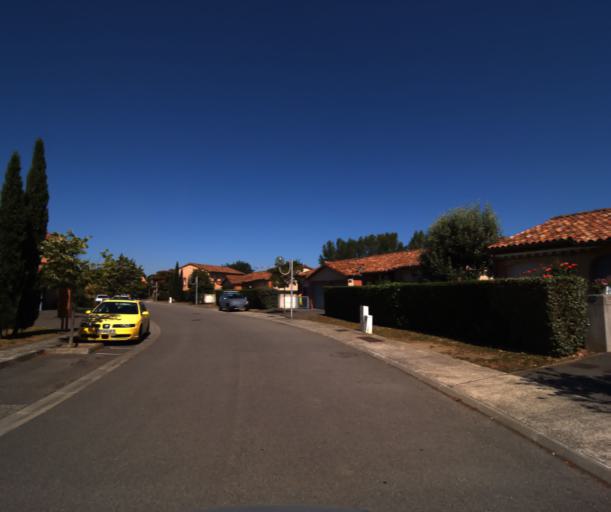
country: FR
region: Midi-Pyrenees
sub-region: Departement de la Haute-Garonne
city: Muret
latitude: 43.4710
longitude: 1.3256
